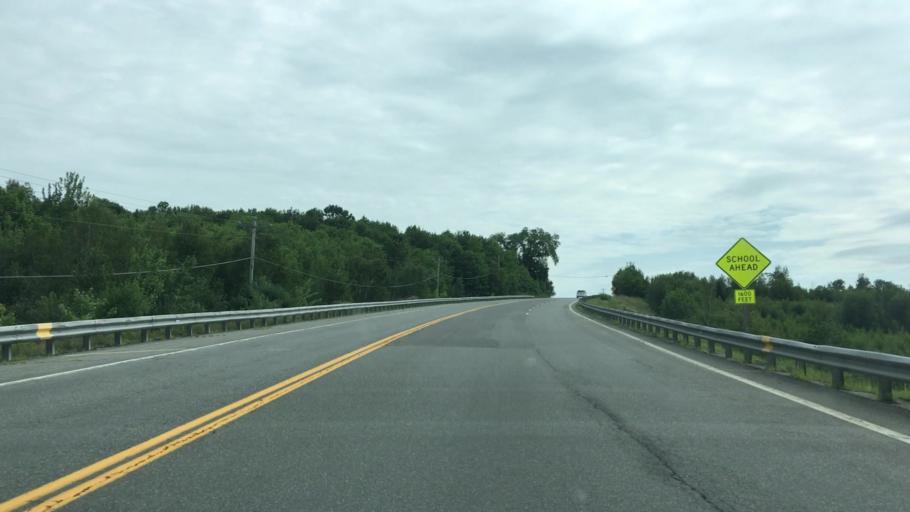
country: US
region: Maine
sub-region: Washington County
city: Calais
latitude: 45.0919
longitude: -67.4837
